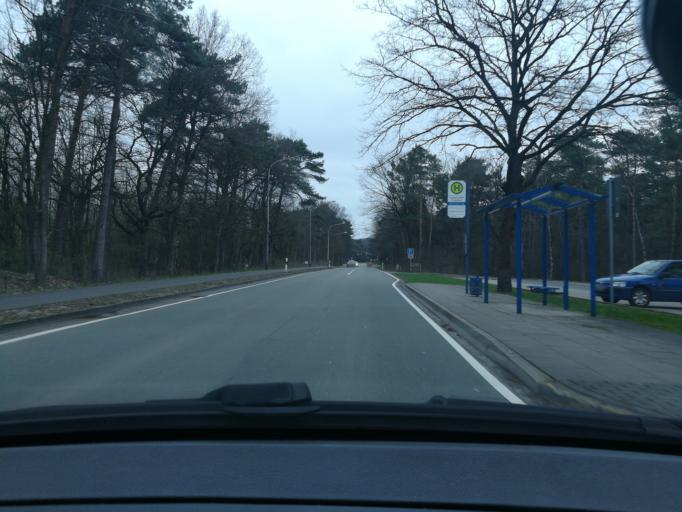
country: DE
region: North Rhine-Westphalia
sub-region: Regierungsbezirk Detmold
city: Oerlinghausen
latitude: 51.9379
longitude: 8.6433
